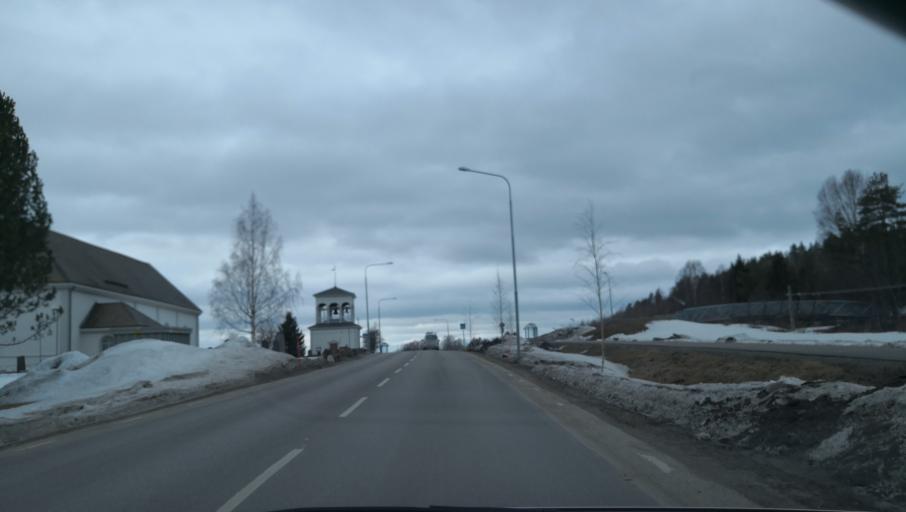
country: SE
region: Vaesterbotten
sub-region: Vannas Kommun
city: Vannasby
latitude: 63.9156
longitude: 19.8058
